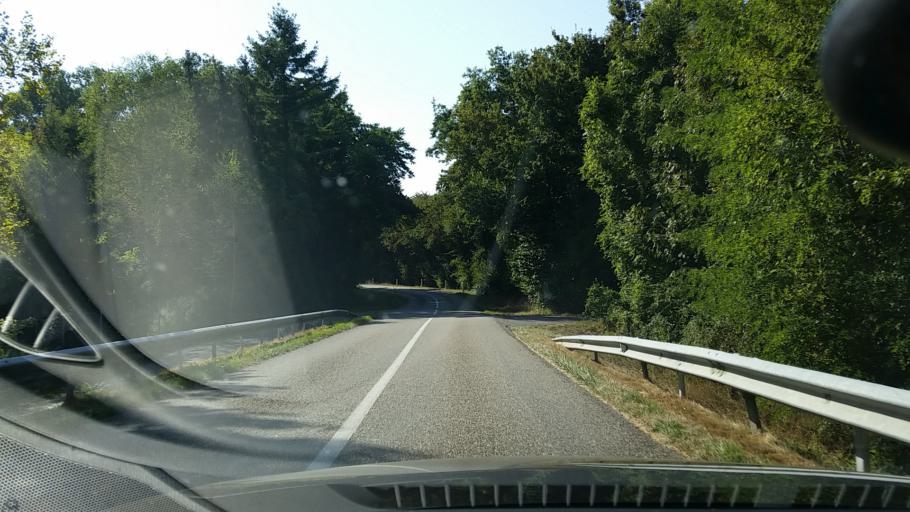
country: FR
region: Alsace
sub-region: Departement du Haut-Rhin
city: Kunheim
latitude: 48.0959
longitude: 7.5310
